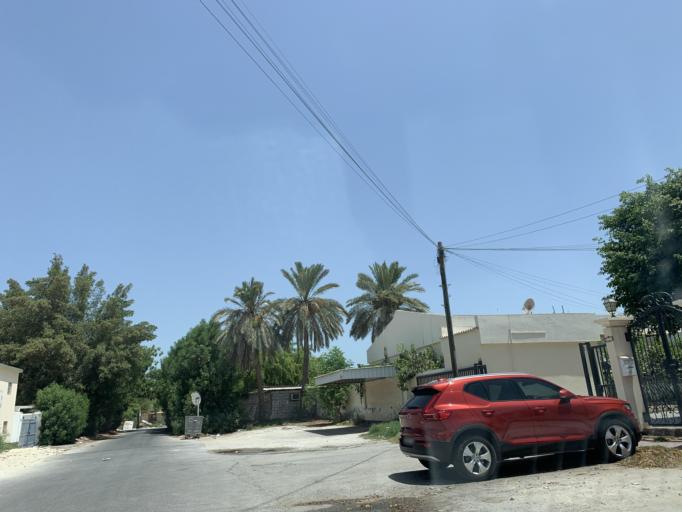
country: BH
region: Manama
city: Jidd Hafs
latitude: 26.2239
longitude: 50.4732
